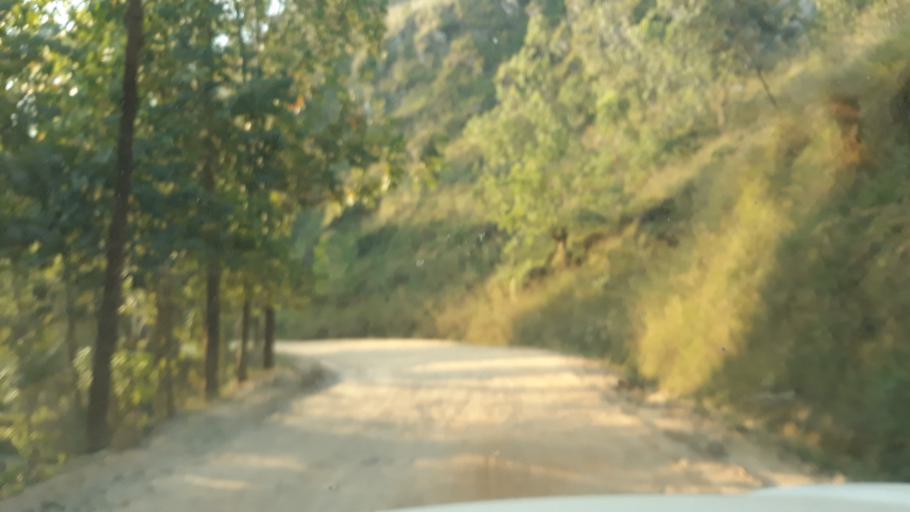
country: RW
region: Western Province
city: Cyangugu
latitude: -2.6945
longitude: 28.8951
